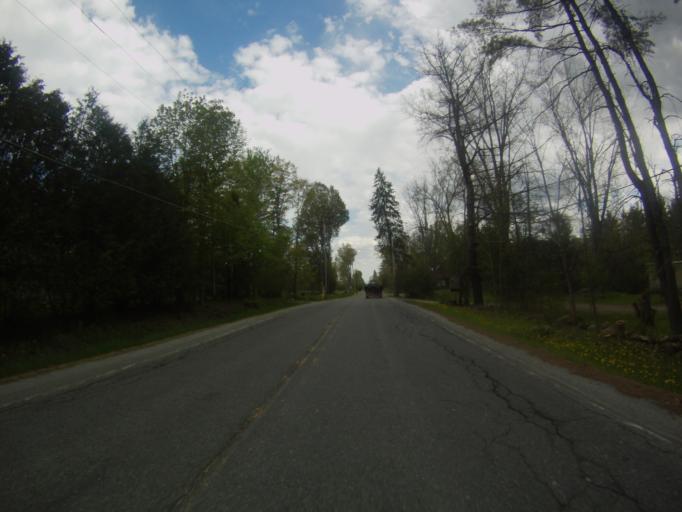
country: US
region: New York
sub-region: Essex County
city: Mineville
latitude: 44.0701
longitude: -73.5208
